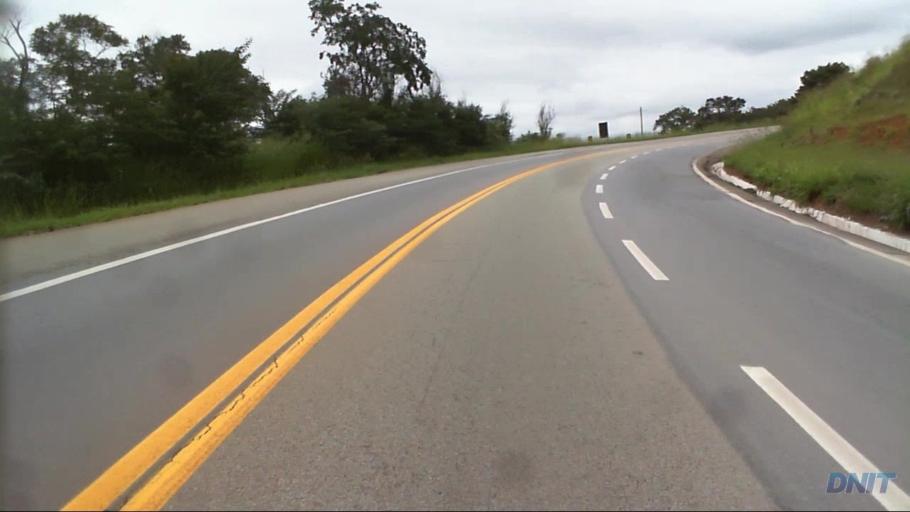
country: BR
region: Minas Gerais
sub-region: Barao De Cocais
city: Barao de Cocais
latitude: -19.7378
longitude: -43.5152
